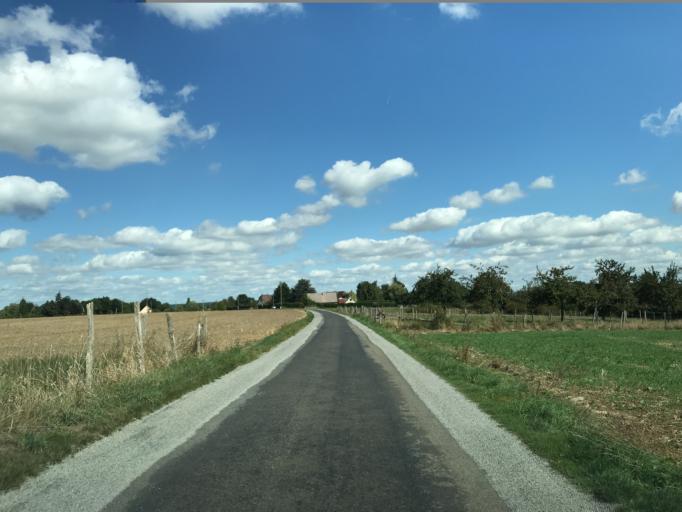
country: FR
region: Haute-Normandie
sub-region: Departement de l'Eure
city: La Chapelle-Reanville
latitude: 49.1311
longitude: 1.3930
